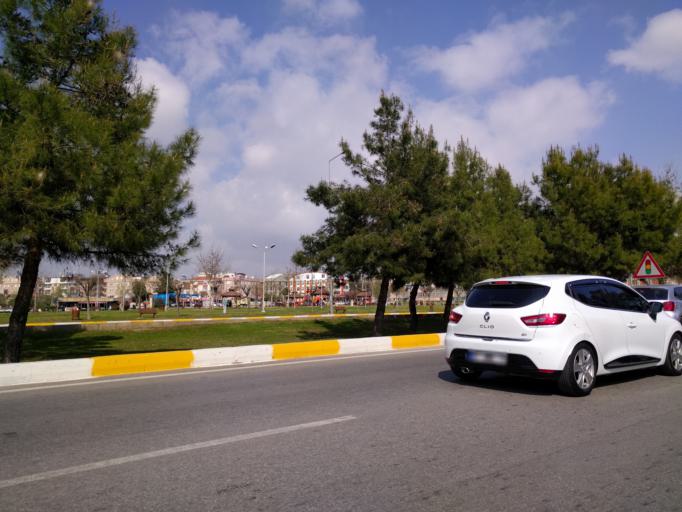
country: TR
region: Antalya
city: Antalya
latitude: 36.9007
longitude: 30.6506
